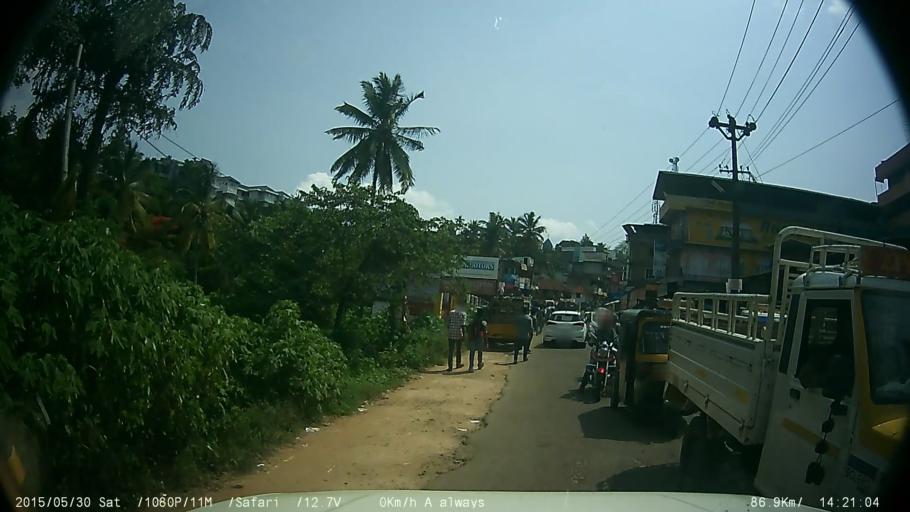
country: IN
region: Kerala
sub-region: Wayanad
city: Panamaram
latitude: 11.8030
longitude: 76.0076
